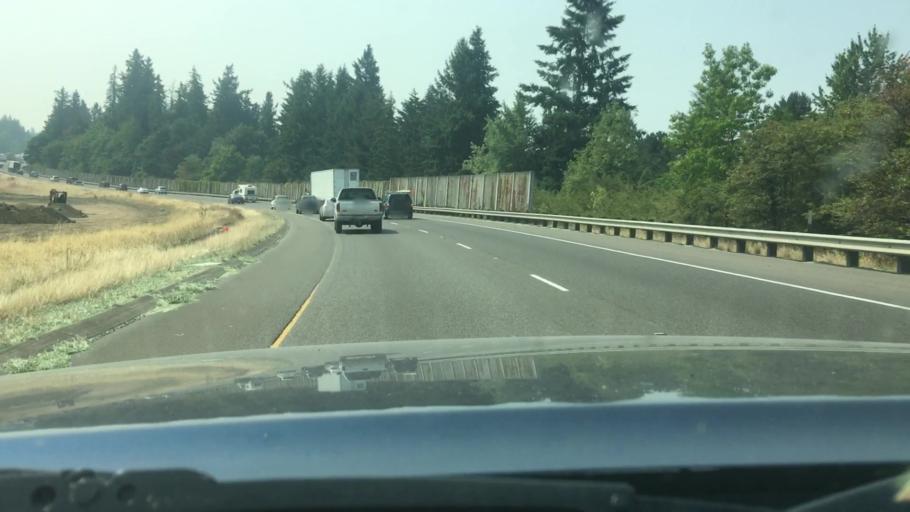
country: US
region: Oregon
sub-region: Washington County
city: Tualatin
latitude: 45.3672
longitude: -122.7600
